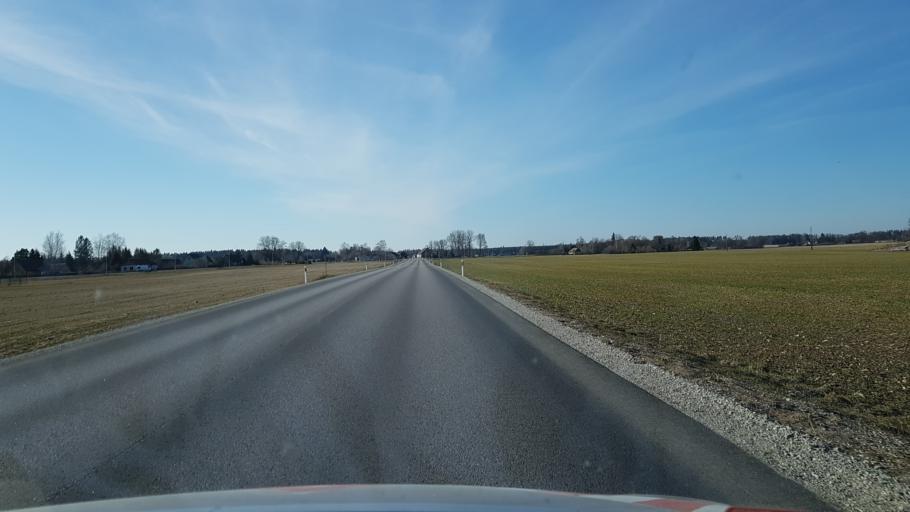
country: EE
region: Laeaene-Virumaa
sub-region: Vinni vald
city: Vinni
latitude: 59.2490
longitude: 26.4743
